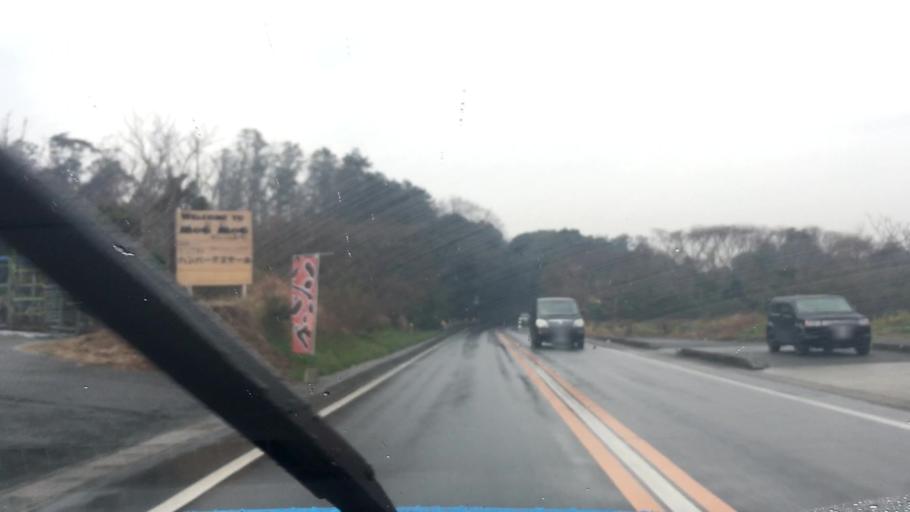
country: JP
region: Aichi
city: Tahara
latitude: 34.6598
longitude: 137.3597
